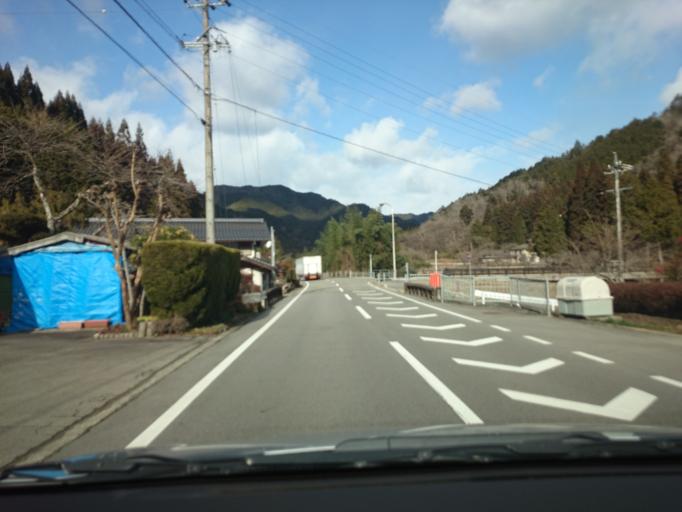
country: JP
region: Gifu
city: Gujo
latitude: 35.7423
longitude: 137.1088
